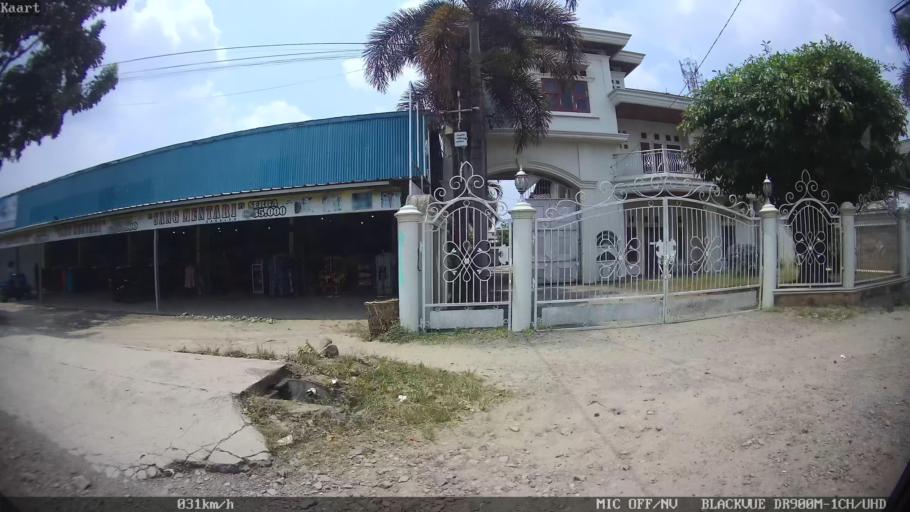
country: ID
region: Lampung
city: Pringsewu
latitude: -5.3593
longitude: 104.9917
